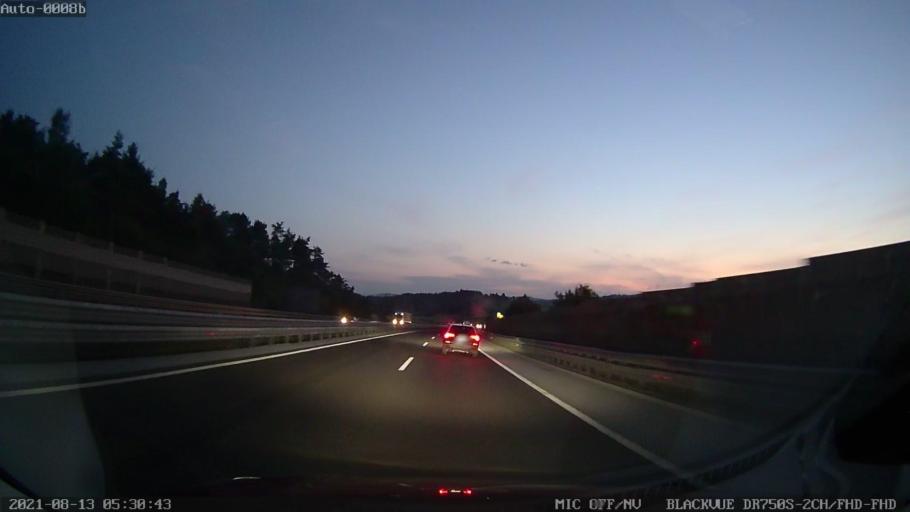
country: SI
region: Cerknica
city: Rakek
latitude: 45.8190
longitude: 14.2842
